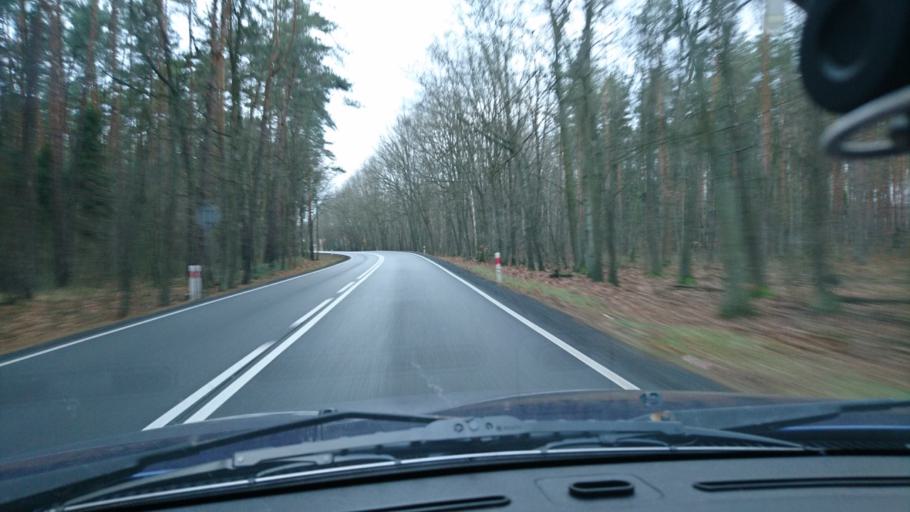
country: PL
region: Opole Voivodeship
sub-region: Powiat kluczborski
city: Kluczbork
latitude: 50.9442
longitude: 18.3219
